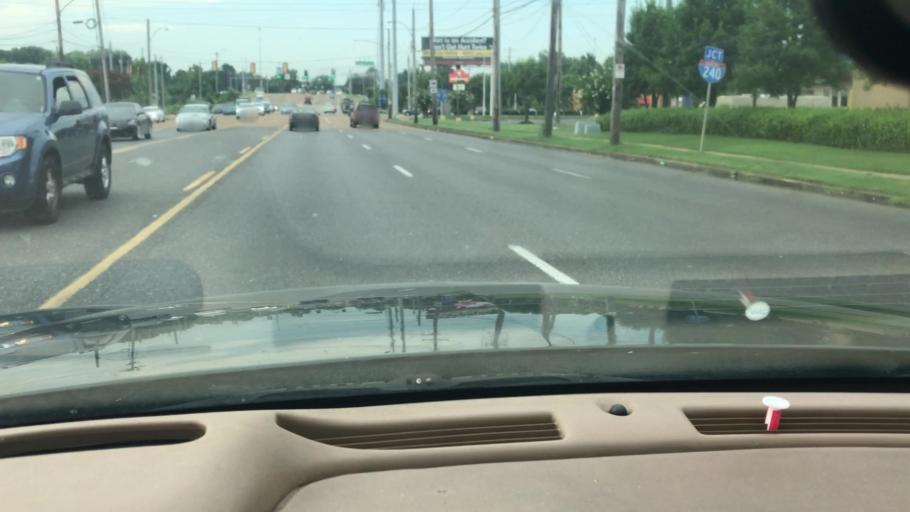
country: US
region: Tennessee
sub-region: Shelby County
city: Germantown
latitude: 35.0747
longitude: -89.9060
